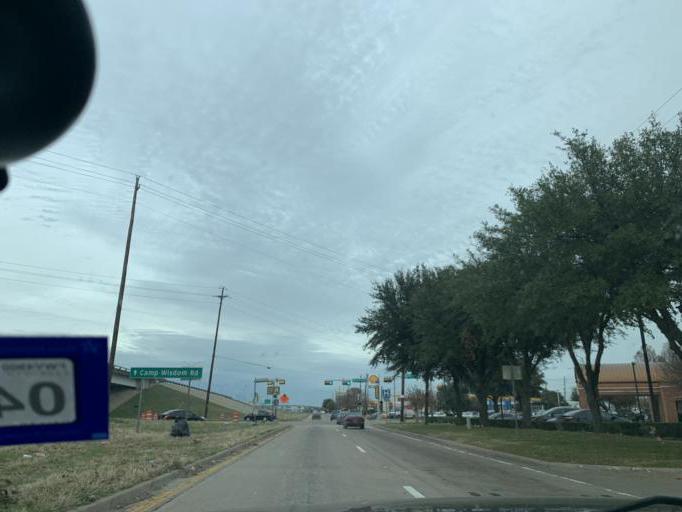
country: US
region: Texas
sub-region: Dallas County
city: Duncanville
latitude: 32.6471
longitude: -96.8845
